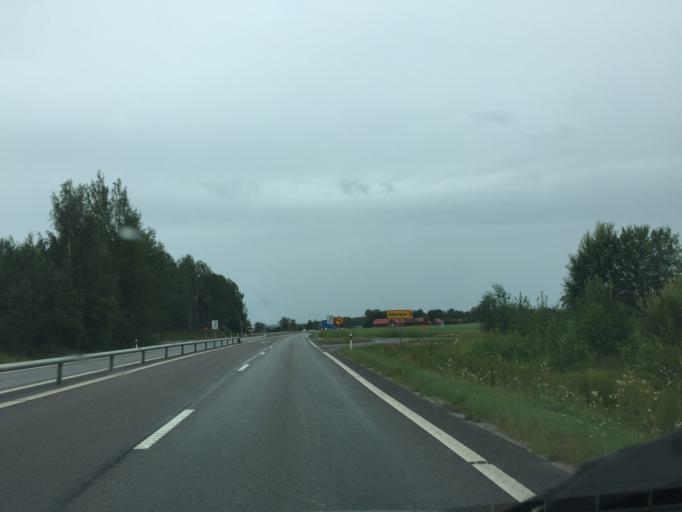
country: SE
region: OErebro
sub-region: Orebro Kommun
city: Orebro
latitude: 59.2015
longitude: 15.2428
